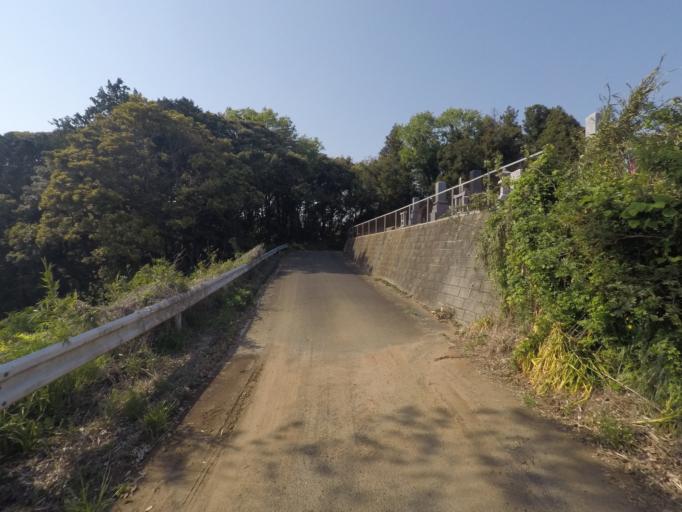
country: JP
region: Ibaraki
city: Inashiki
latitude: 36.0570
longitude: 140.4445
